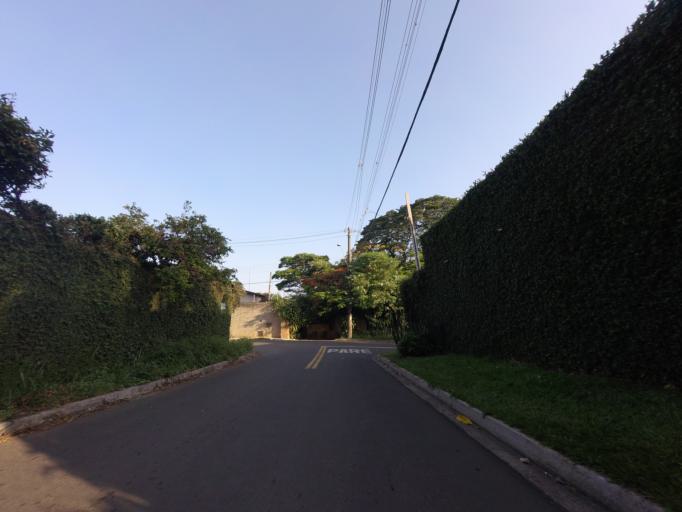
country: BR
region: Sao Paulo
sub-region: Piracicaba
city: Piracicaba
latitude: -22.7462
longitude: -47.6066
